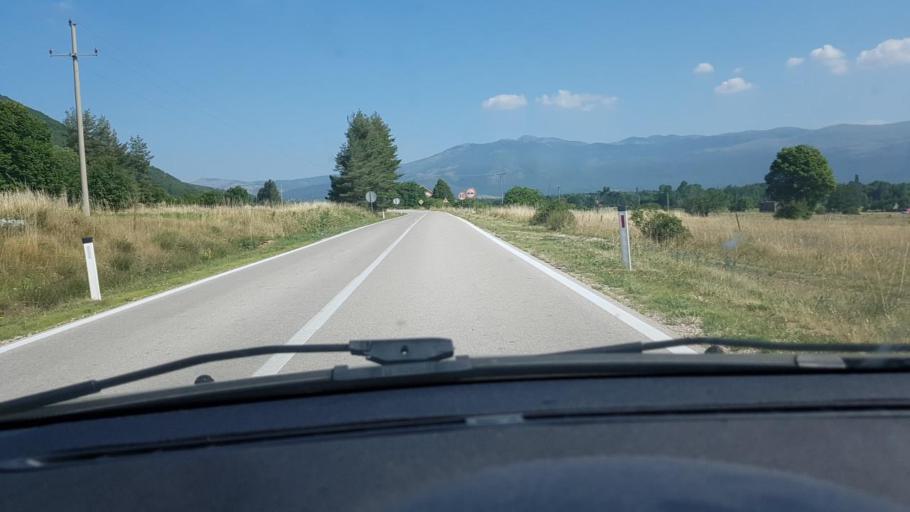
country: BA
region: Federation of Bosnia and Herzegovina
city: Glamoc
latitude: 44.0351
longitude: 16.5954
